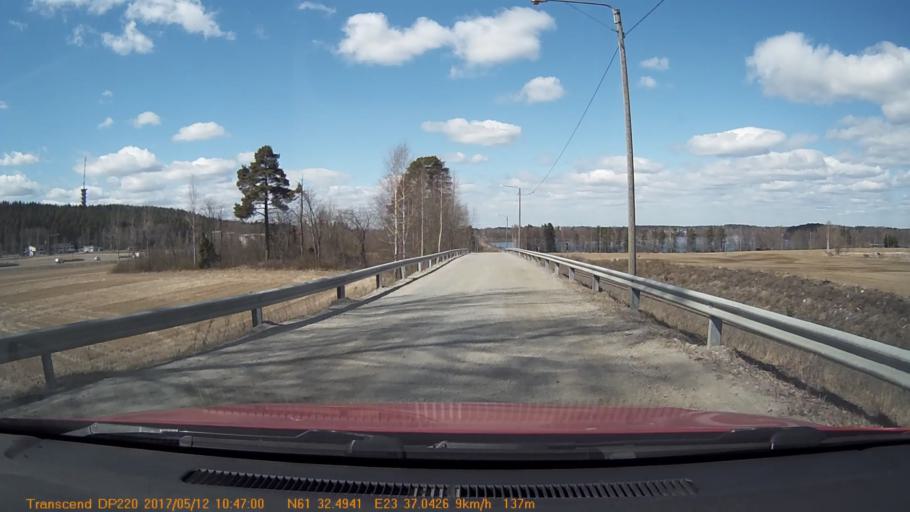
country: FI
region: Pirkanmaa
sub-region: Tampere
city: Yloejaervi
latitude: 61.5415
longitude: 23.6175
